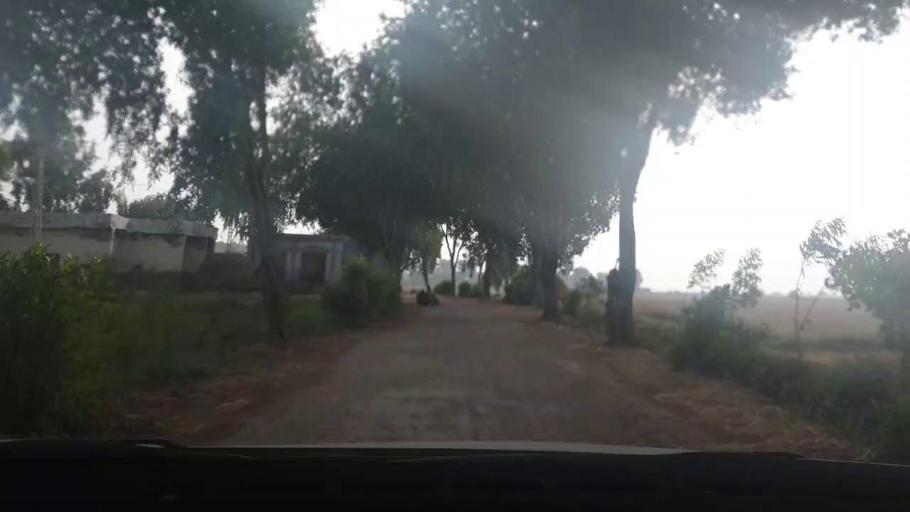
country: PK
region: Sindh
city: Tando Muhammad Khan
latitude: 25.1108
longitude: 68.5400
